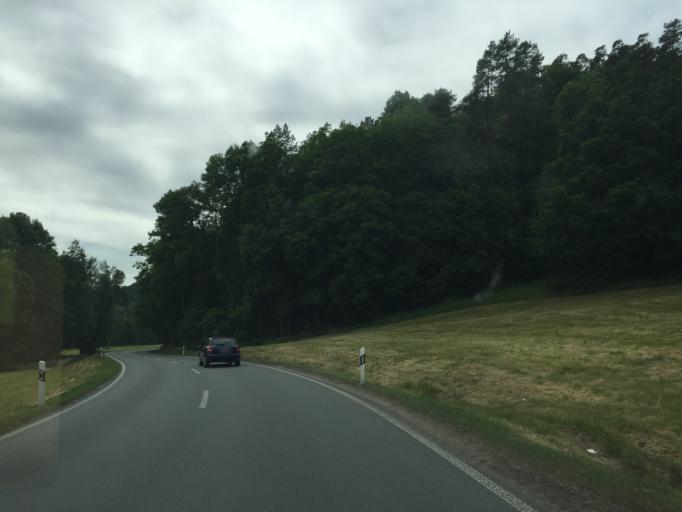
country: DE
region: Thuringia
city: Bad Blankenburg
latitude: 50.6956
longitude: 11.2210
